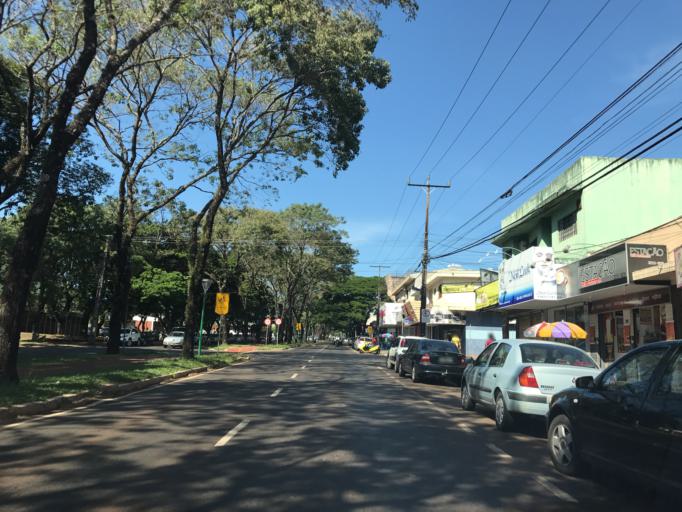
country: BR
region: Parana
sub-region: Maringa
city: Maringa
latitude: -23.4088
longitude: -51.9561
